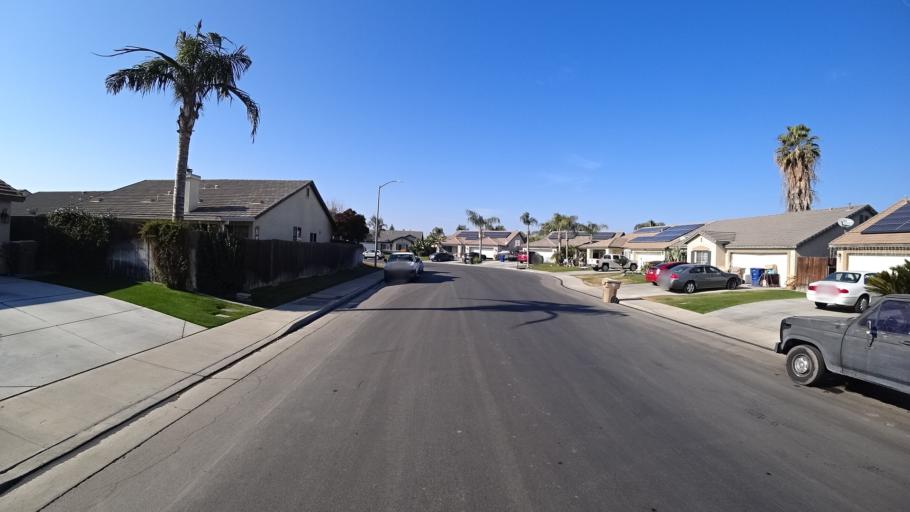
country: US
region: California
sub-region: Kern County
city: Greenacres
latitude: 35.3146
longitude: -119.1224
